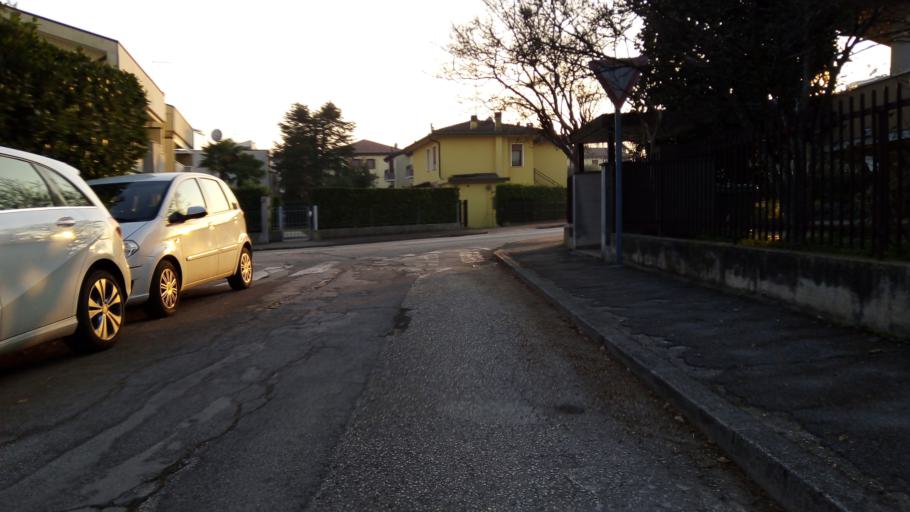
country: IT
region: Veneto
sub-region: Provincia di Padova
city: Abano Terme
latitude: 45.3554
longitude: 11.7621
